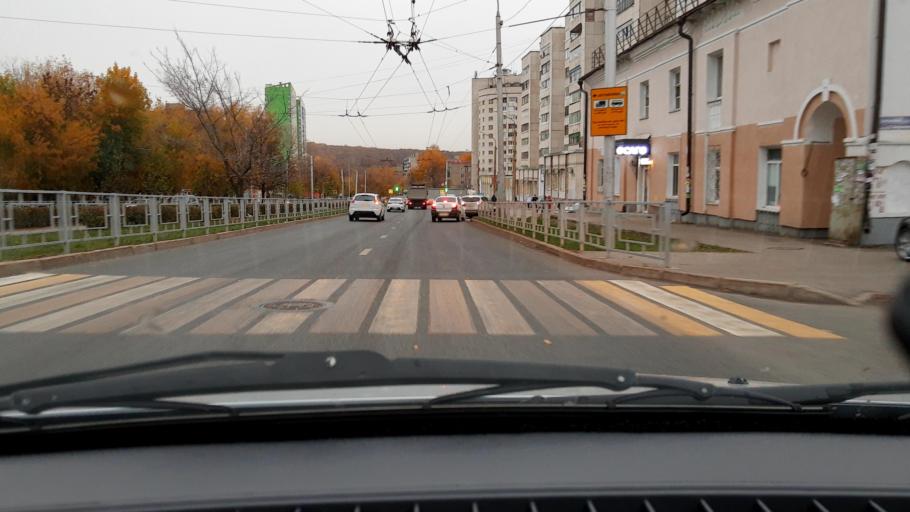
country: RU
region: Bashkortostan
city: Ufa
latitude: 54.8123
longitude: 56.1248
